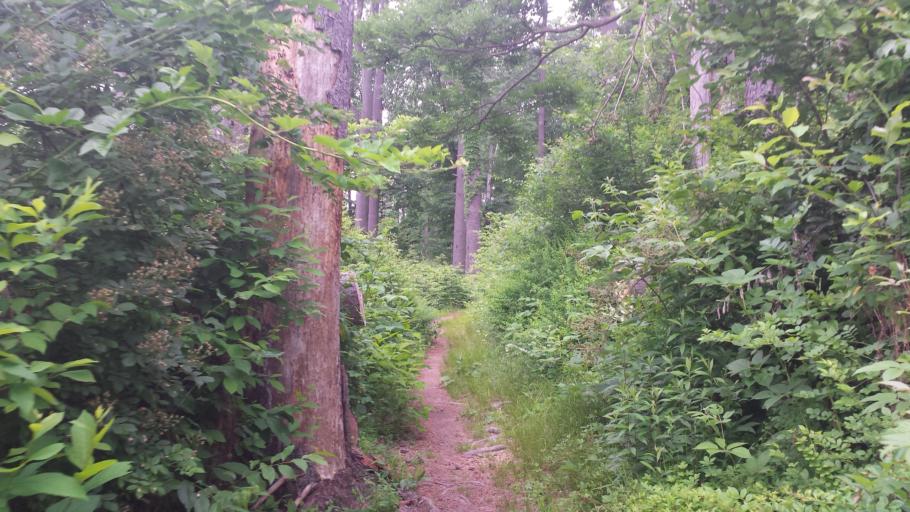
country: US
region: New York
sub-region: Westchester County
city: Pound Ridge
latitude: 41.2627
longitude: -73.5979
